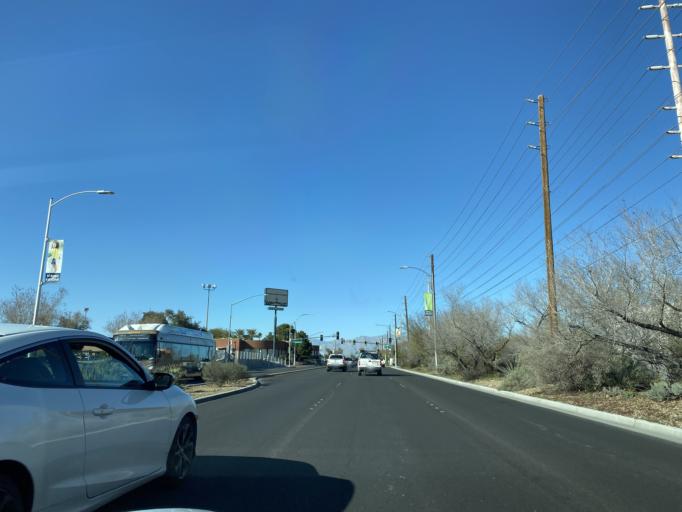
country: US
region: Nevada
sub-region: Clark County
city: Las Vegas
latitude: 36.1688
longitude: -115.1925
